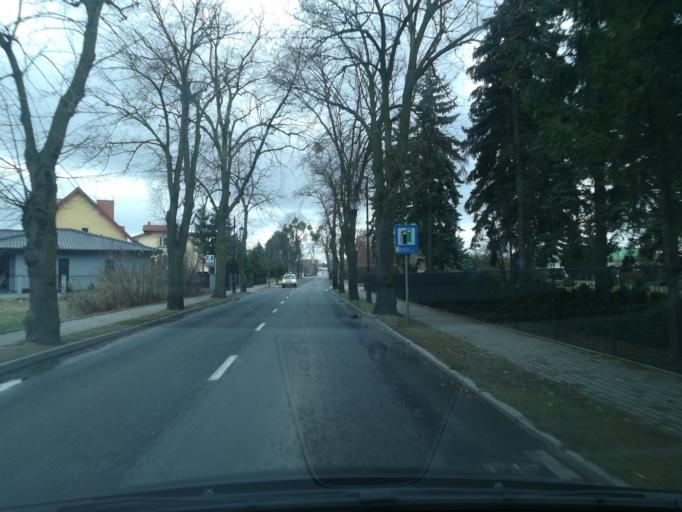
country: PL
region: Kujawsko-Pomorskie
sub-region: Powiat aleksandrowski
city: Ciechocinek
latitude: 52.8762
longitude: 18.7775
